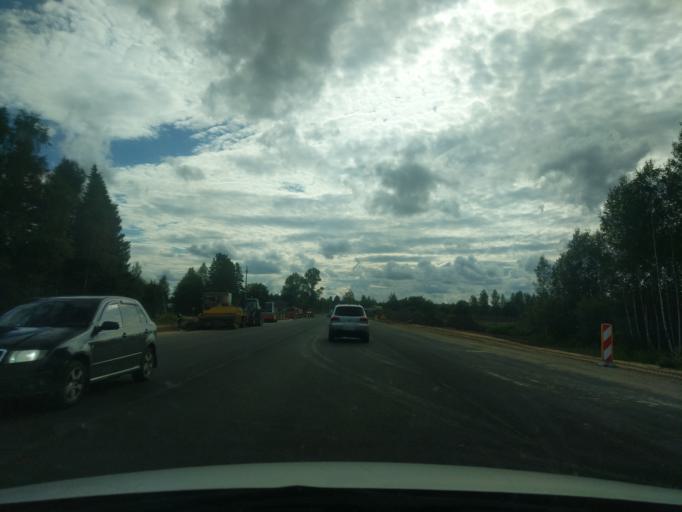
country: RU
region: Jaroslavl
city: Levashevo
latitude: 57.6593
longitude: 40.5668
